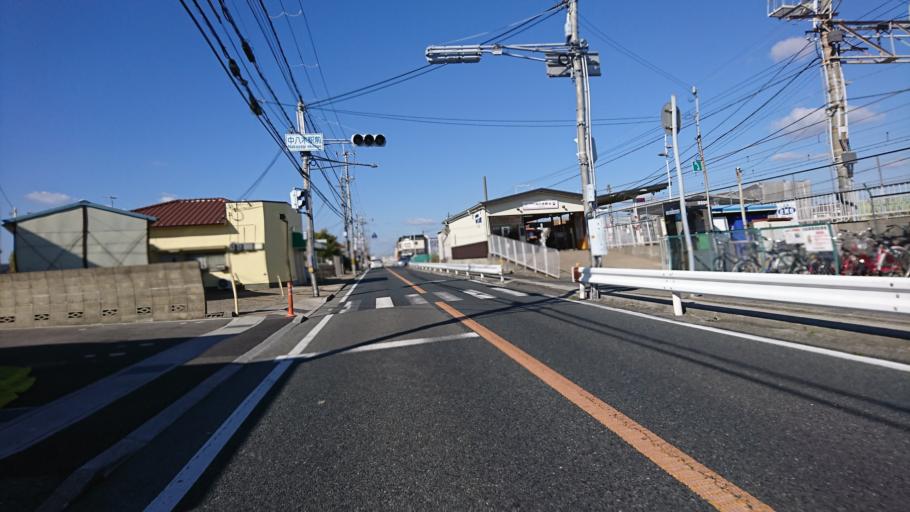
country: JP
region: Hyogo
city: Akashi
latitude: 34.6704
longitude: 134.9364
